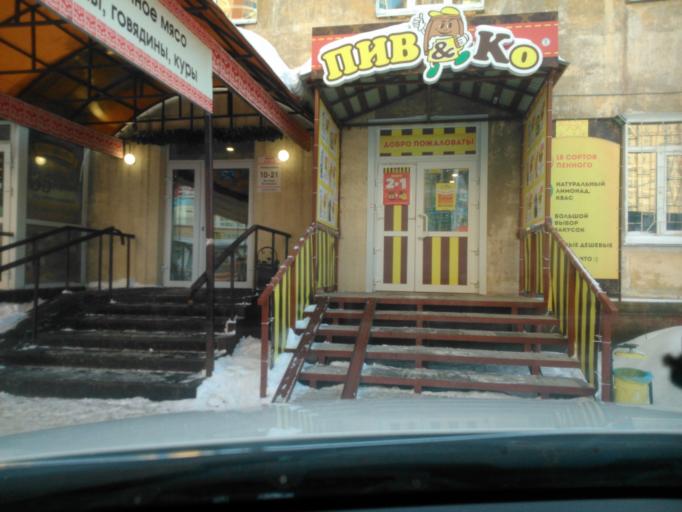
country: RU
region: Perm
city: Perm
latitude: 58.0015
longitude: 56.3038
